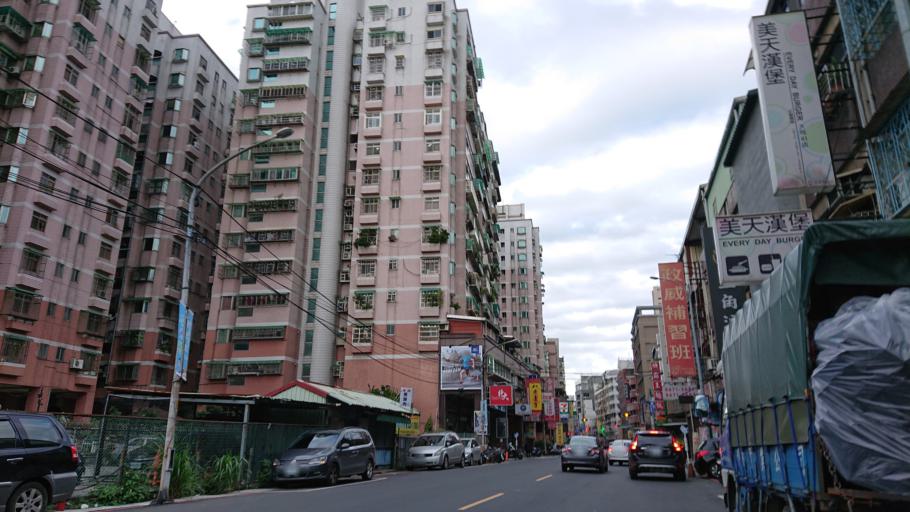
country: TW
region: Taiwan
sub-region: Taoyuan
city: Taoyuan
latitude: 24.9271
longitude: 121.3749
